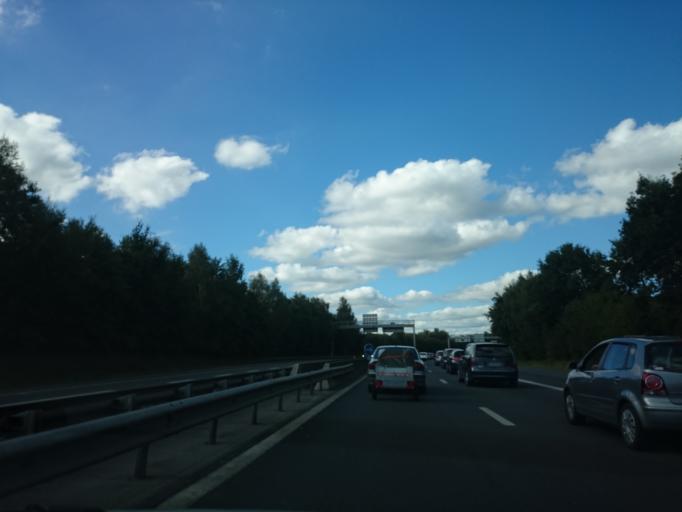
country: FR
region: Pays de la Loire
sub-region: Departement de la Loire-Atlantique
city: Orvault
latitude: 47.2536
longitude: -1.6217
